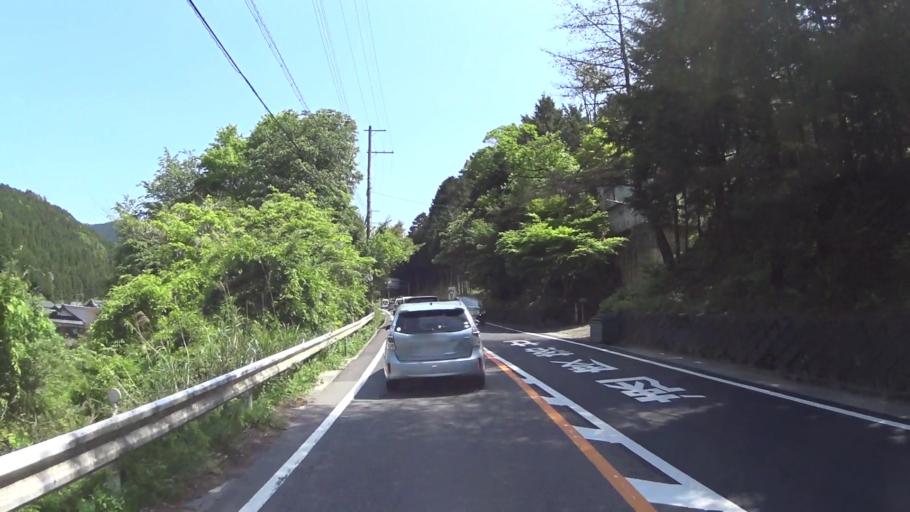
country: JP
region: Shiga Prefecture
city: Kitahama
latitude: 35.1460
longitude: 135.8417
